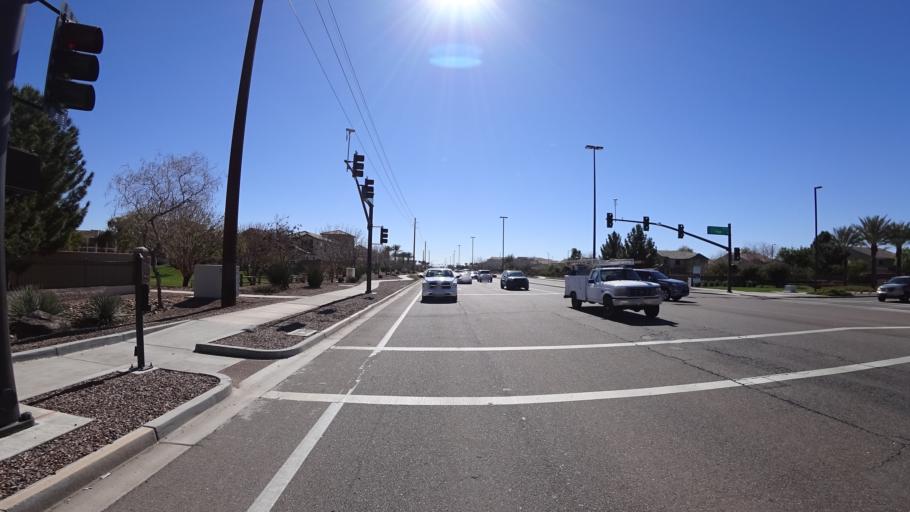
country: US
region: Arizona
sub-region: Maricopa County
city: Gilbert
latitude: 33.2994
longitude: -111.7555
